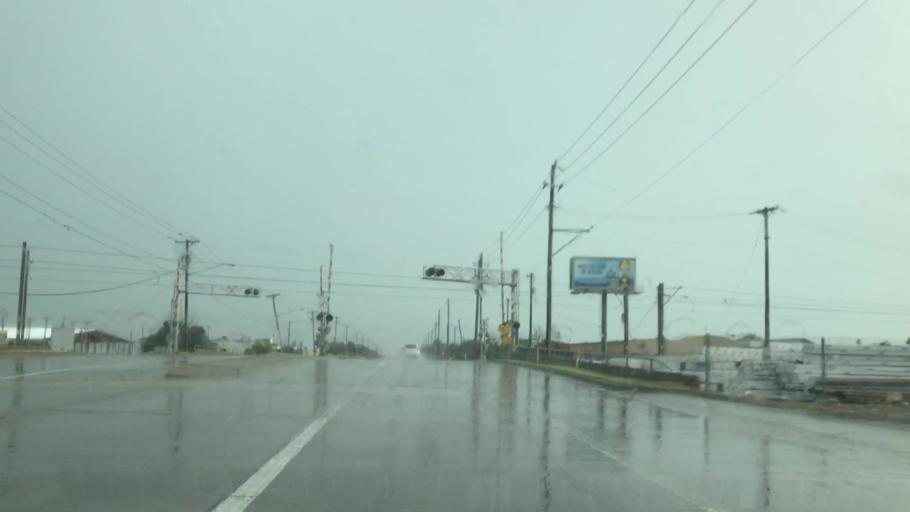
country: US
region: Texas
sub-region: Dallas County
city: Richardson
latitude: 32.9022
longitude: -96.7006
